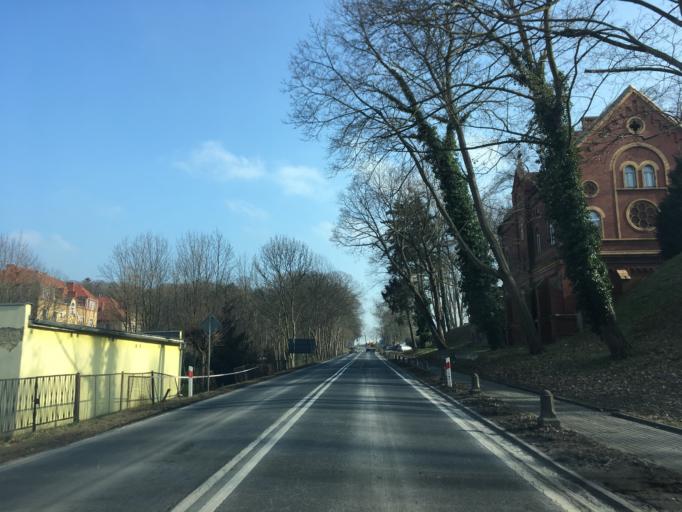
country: PL
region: Lower Silesian Voivodeship
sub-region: Powiat legnicki
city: Chojnow
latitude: 51.2669
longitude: 15.9286
